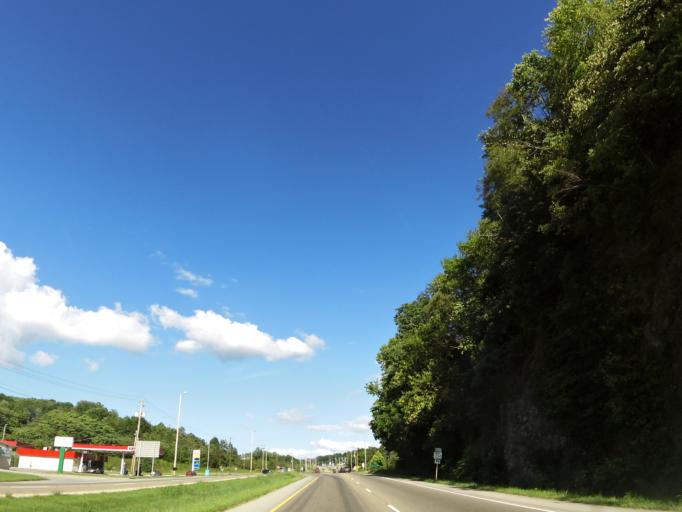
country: US
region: Tennessee
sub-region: Greene County
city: Greeneville
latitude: 36.1725
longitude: -82.8524
